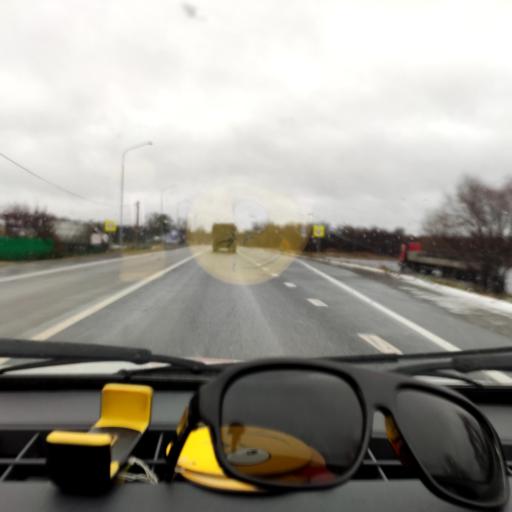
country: RU
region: Bashkortostan
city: Urman
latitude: 54.8235
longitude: 56.8880
